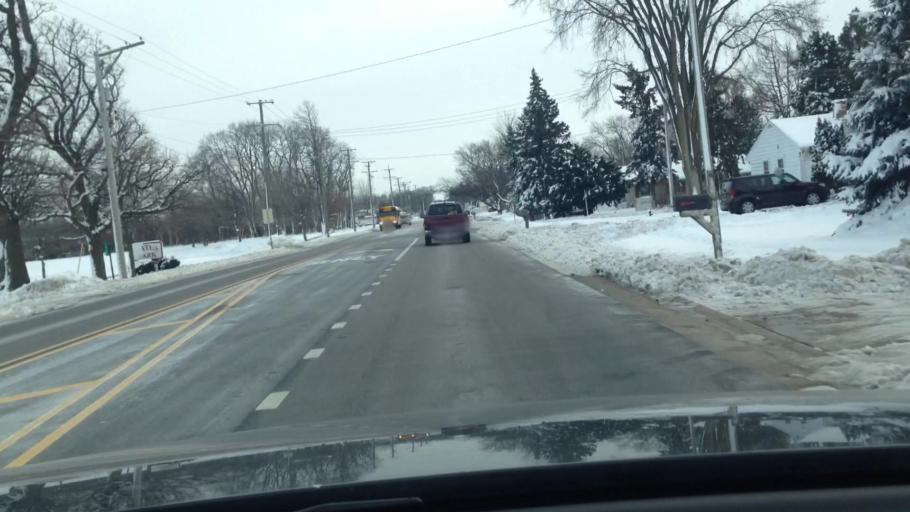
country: US
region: Illinois
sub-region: McHenry County
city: Woodstock
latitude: 42.3311
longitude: -88.4432
